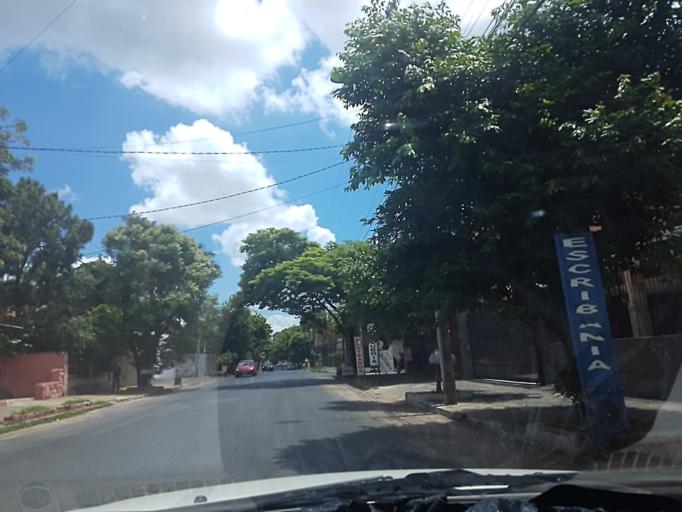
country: PY
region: Central
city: Lambare
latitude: -25.3196
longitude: -57.5730
